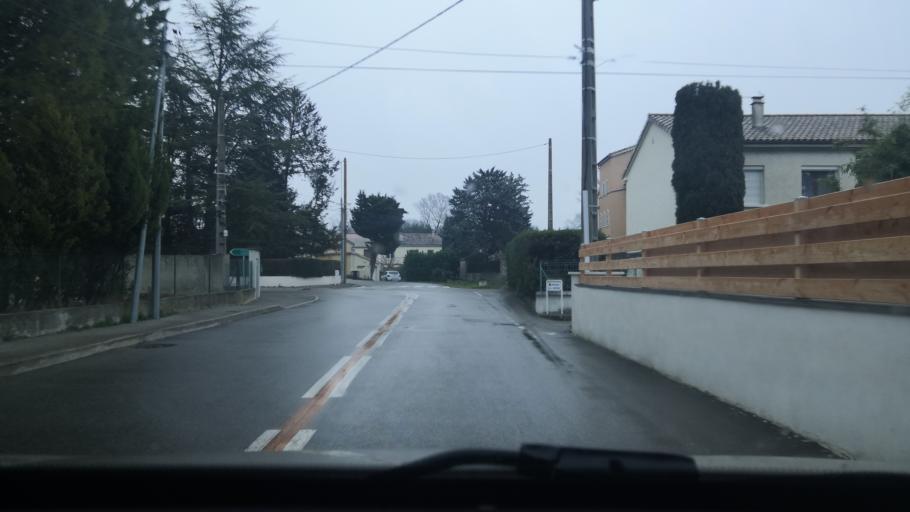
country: FR
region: Rhone-Alpes
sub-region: Departement de la Drome
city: Montelimar
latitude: 44.5519
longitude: 4.7547
